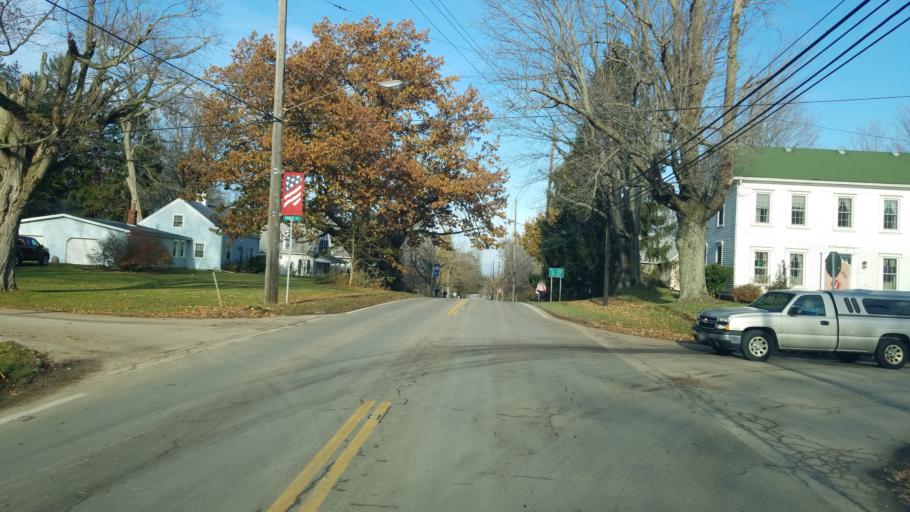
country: US
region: Ohio
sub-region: Ashtabula County
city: North Kingsville
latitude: 41.8906
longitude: -80.6764
